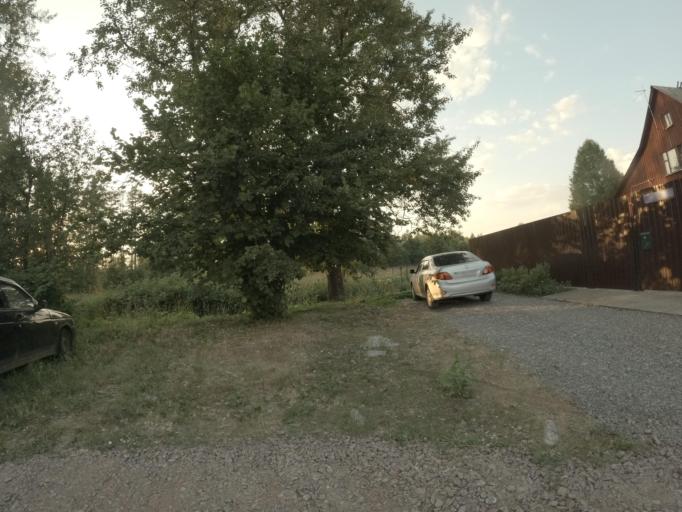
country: RU
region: Leningrad
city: Pavlovo
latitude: 59.8519
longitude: 30.9314
